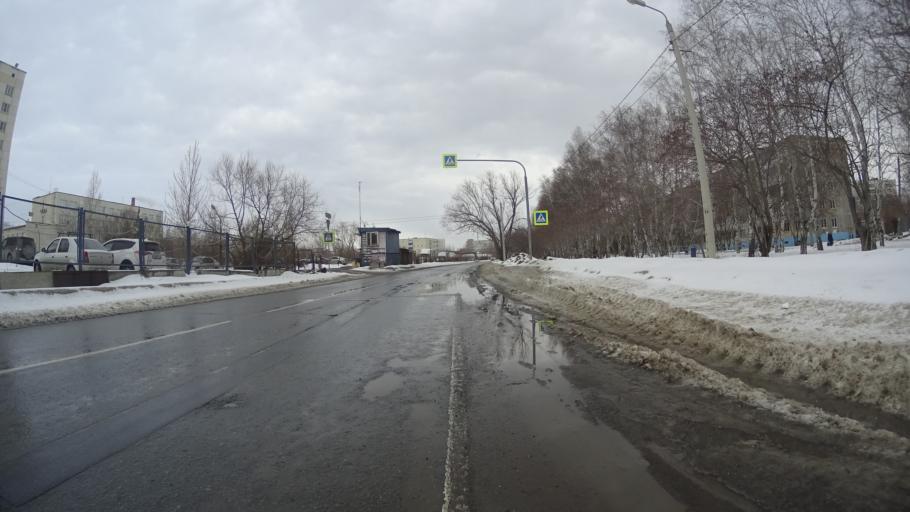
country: RU
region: Chelyabinsk
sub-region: Gorod Chelyabinsk
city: Chelyabinsk
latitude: 55.2002
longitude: 61.3232
